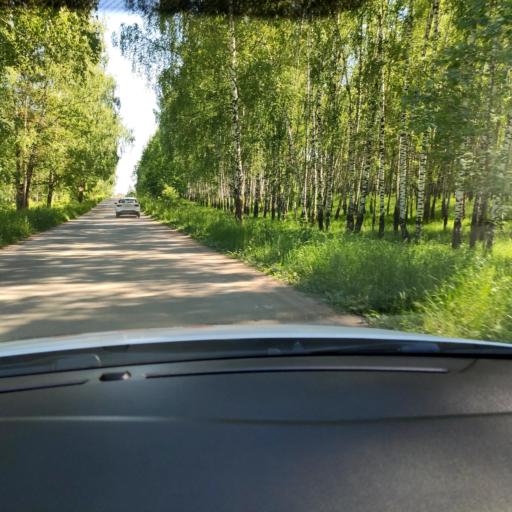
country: RU
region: Tatarstan
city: Staroye Arakchino
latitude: 55.8897
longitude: 49.0323
